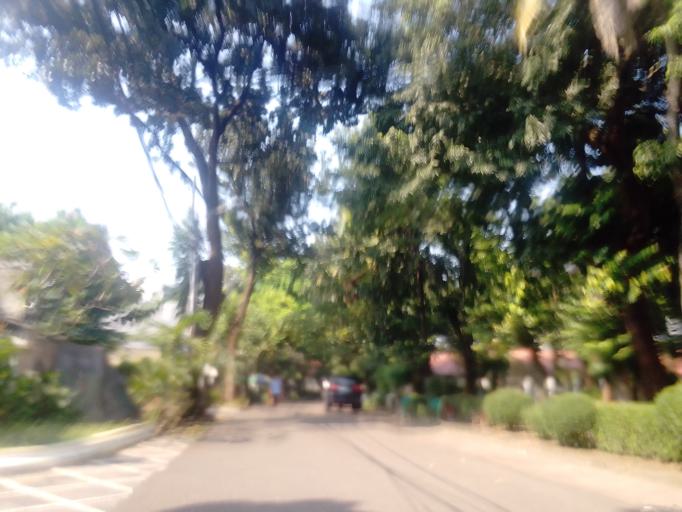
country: ID
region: Jakarta Raya
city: Jakarta
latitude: -6.2539
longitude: 106.8074
